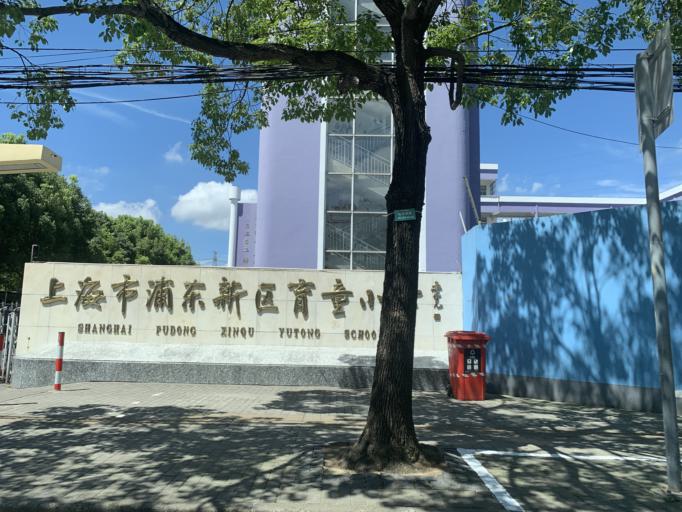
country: CN
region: Shanghai Shi
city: Huamu
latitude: 31.1734
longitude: 121.5362
